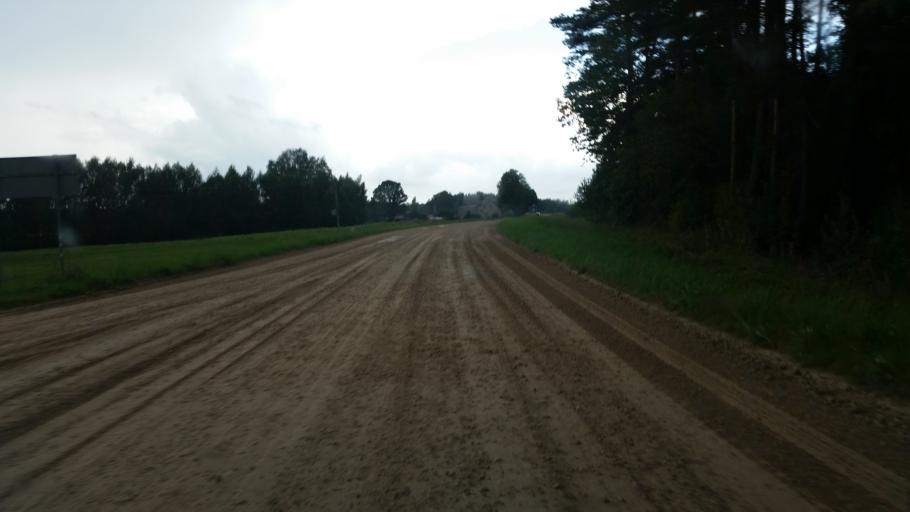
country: LV
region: Vecumnieki
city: Vecumnieki
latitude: 56.4231
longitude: 24.4974
